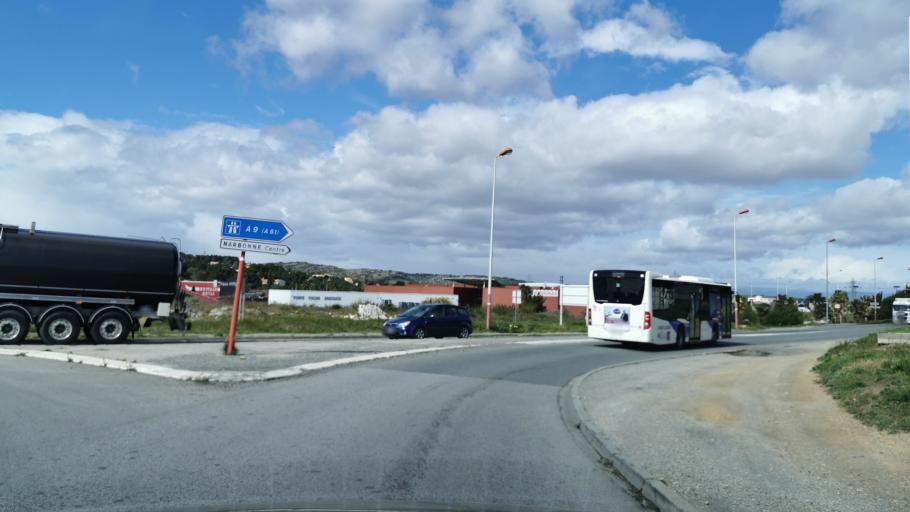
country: FR
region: Languedoc-Roussillon
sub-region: Departement de l'Aude
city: Narbonne
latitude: 43.1628
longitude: 2.9889
